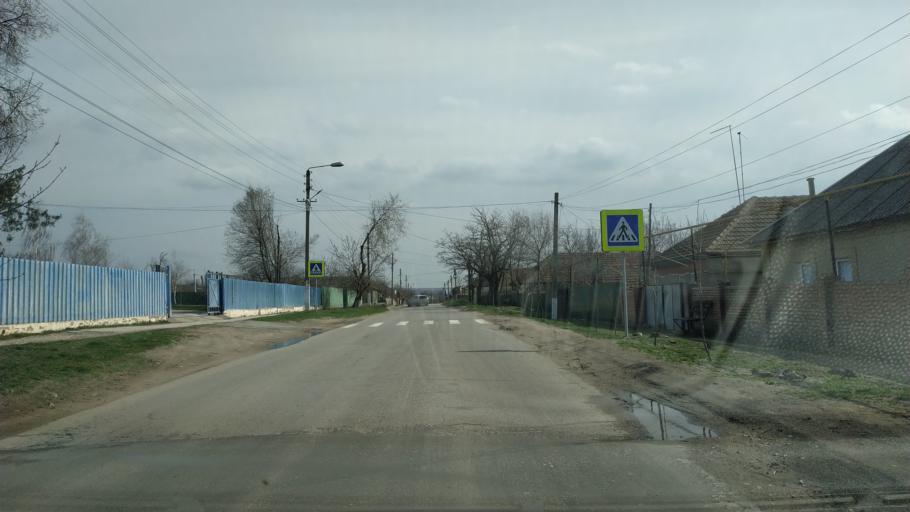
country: MD
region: Gagauzia
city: Vulcanesti
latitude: 45.6745
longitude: 28.4181
